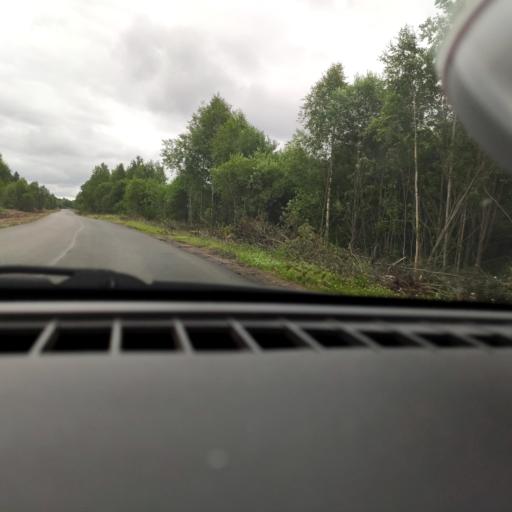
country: RU
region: Perm
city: Polazna
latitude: 58.3356
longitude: 56.1887
